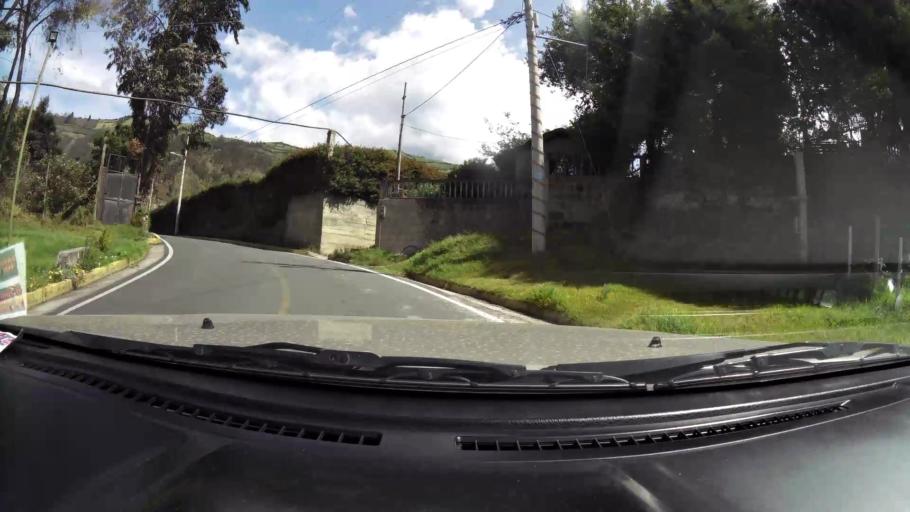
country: EC
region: Chimborazo
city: Guano
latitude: -1.5666
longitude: -78.5329
